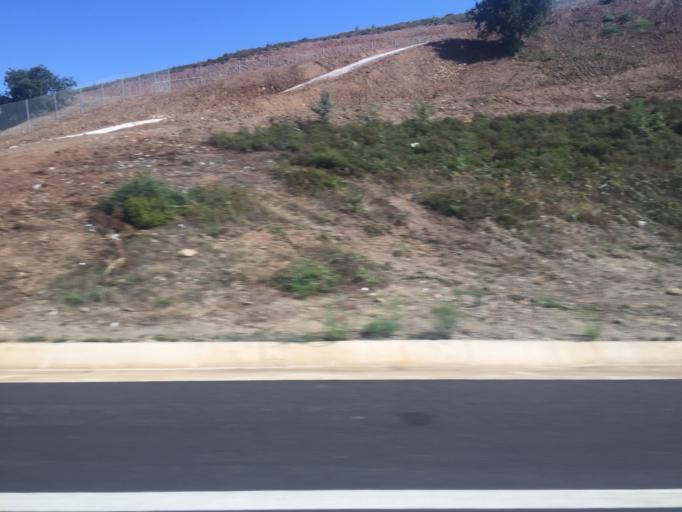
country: TR
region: Bursa
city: Mahmudiye
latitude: 40.2757
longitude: 28.5481
